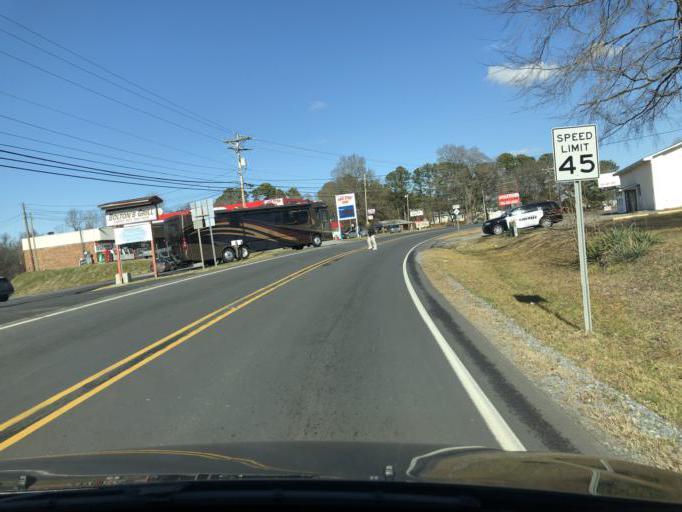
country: US
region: North Carolina
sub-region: Cleveland County
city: Shelby
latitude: 35.2243
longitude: -81.5288
